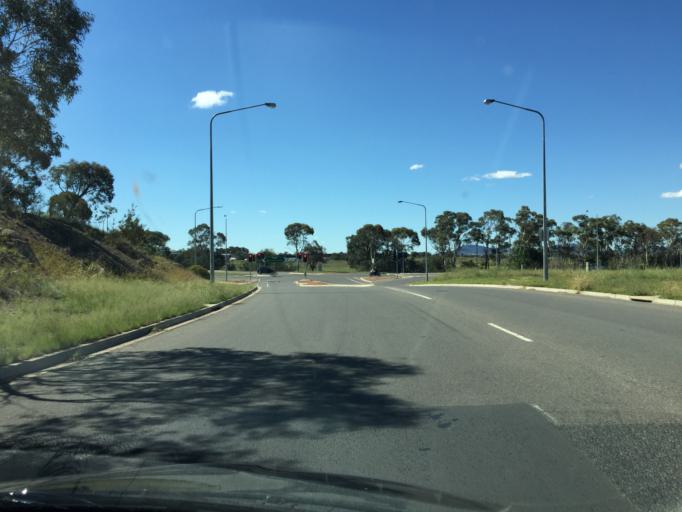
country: AU
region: Australian Capital Territory
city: Macarthur
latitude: -35.3837
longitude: 149.1749
